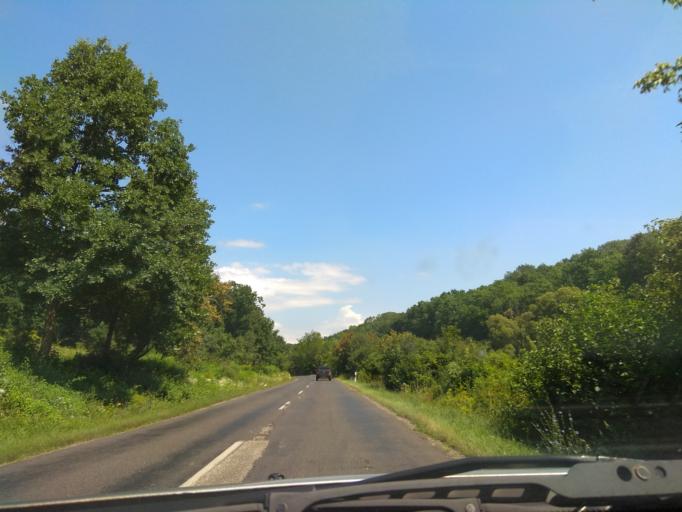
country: HU
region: Borsod-Abauj-Zemplen
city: Harsany
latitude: 48.0079
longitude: 20.7624
